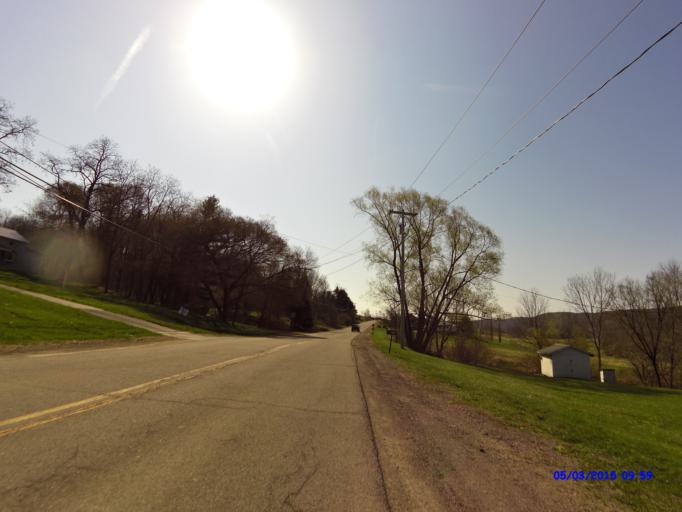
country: US
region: New York
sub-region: Cattaraugus County
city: Franklinville
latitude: 42.3313
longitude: -78.4424
